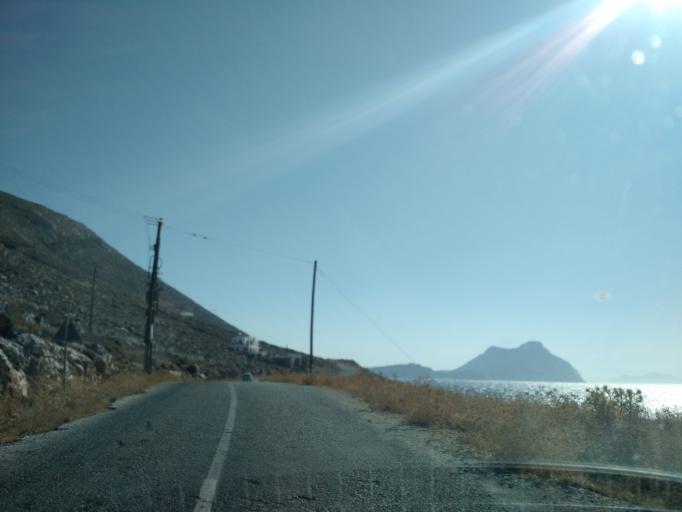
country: GR
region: South Aegean
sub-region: Nomos Kykladon
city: Amorgos
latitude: 36.8957
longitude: 25.9686
